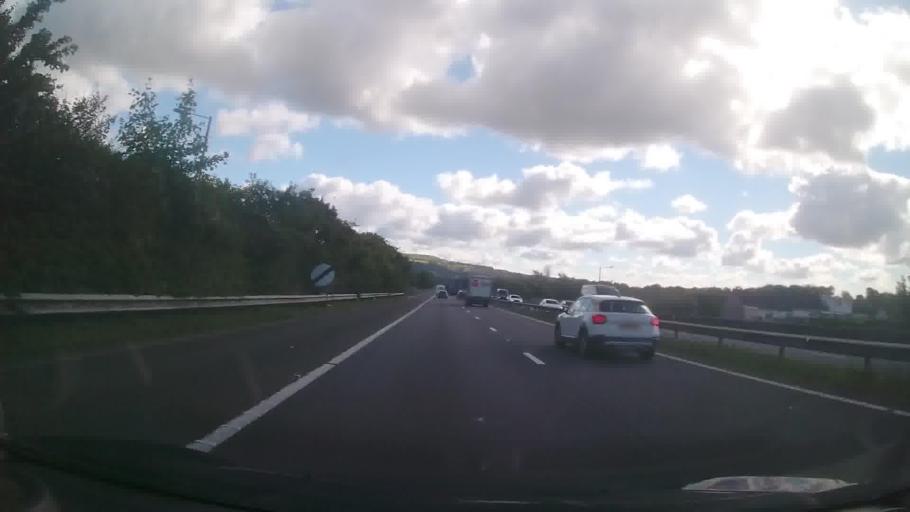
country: GB
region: Wales
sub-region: City and County of Swansea
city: Morriston
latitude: 51.6785
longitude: -3.9156
